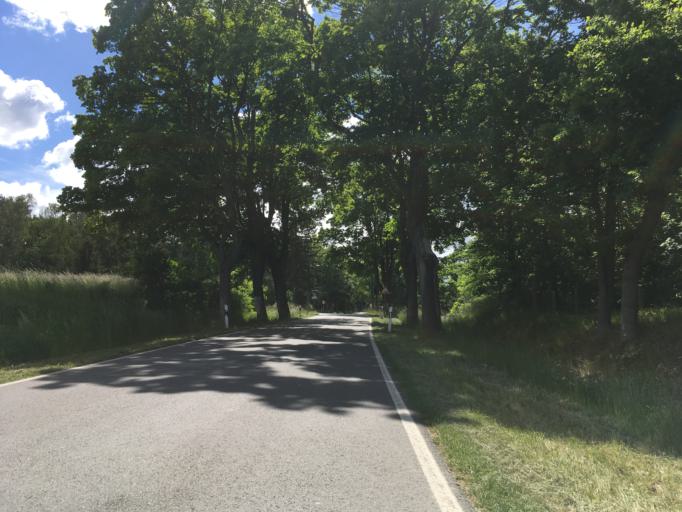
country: DE
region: Brandenburg
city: Protzel
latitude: 52.6767
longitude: 14.0007
